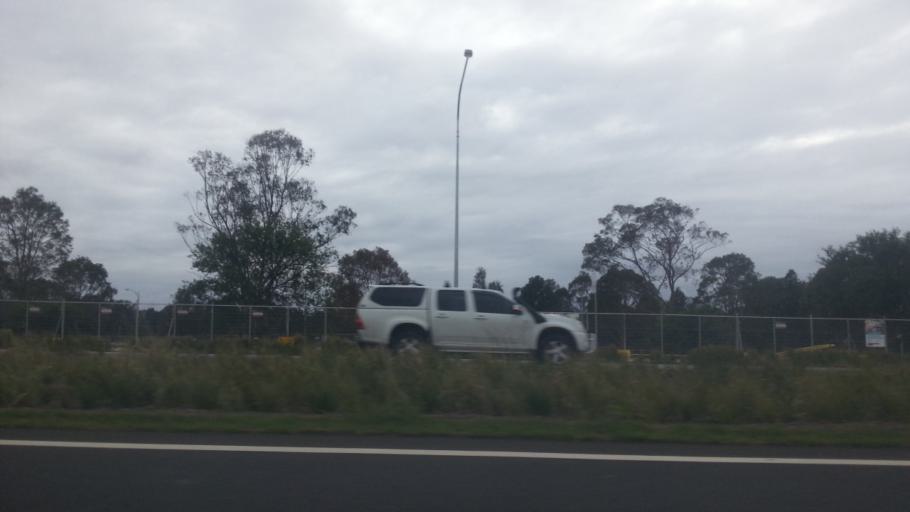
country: AU
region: New South Wales
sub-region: Camden
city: Narellan
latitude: -34.0311
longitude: 150.7287
